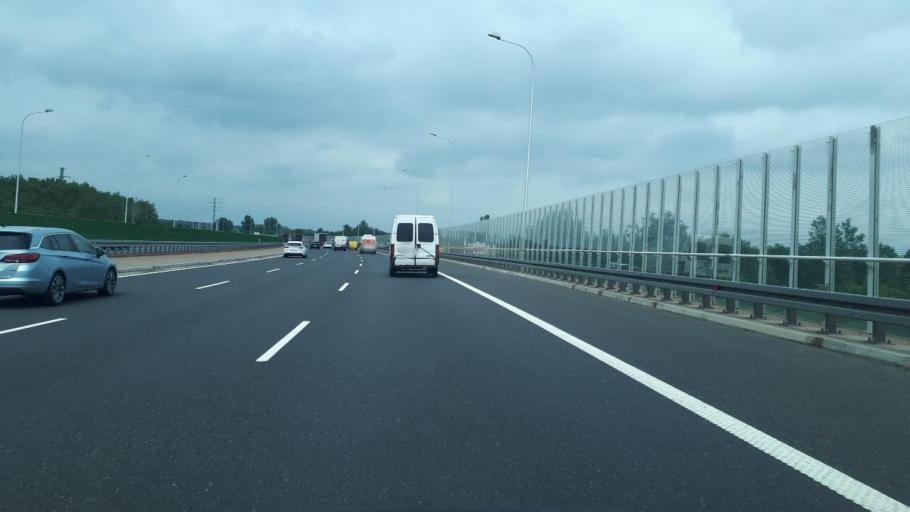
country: PL
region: Silesian Voivodeship
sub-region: Gliwice
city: Gliwice
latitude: 50.2983
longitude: 18.7246
